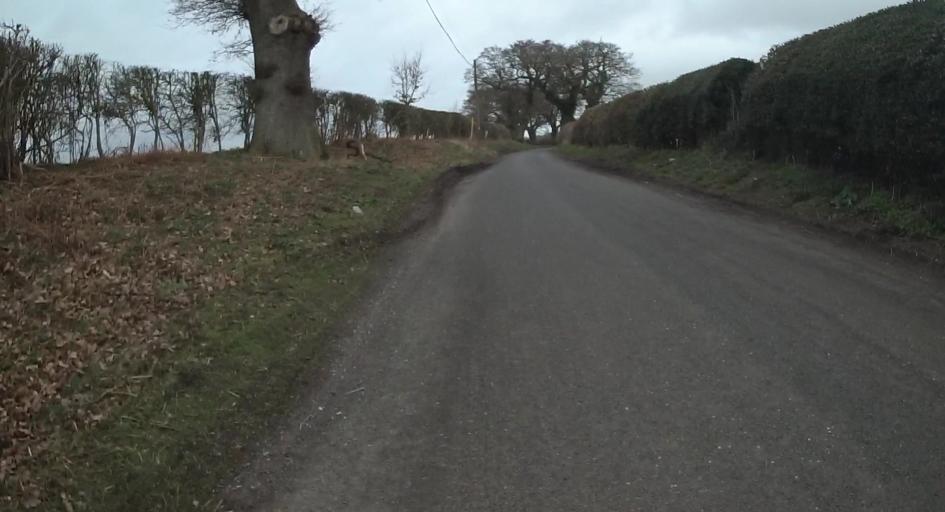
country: GB
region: England
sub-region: Hampshire
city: Overton
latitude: 51.2568
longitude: -1.1937
